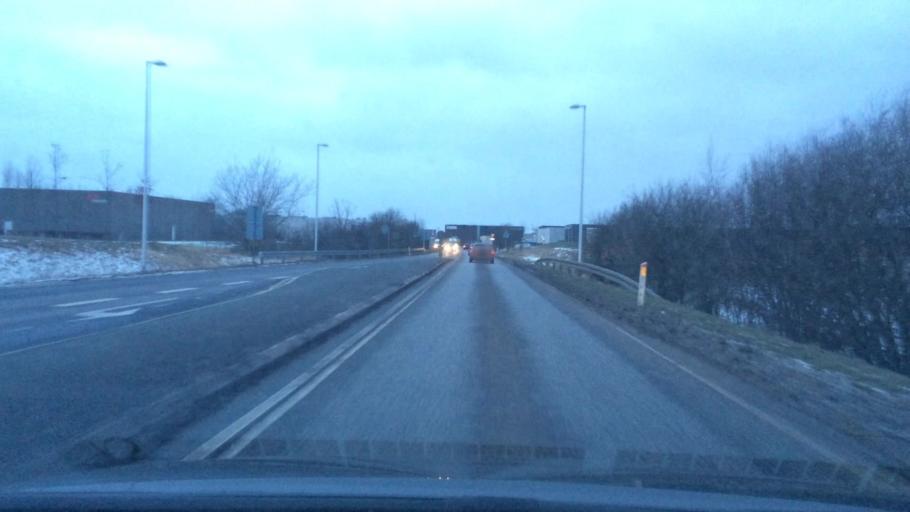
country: DK
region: Central Jutland
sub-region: Horsens Kommune
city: Horsens
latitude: 55.8322
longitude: 9.8038
